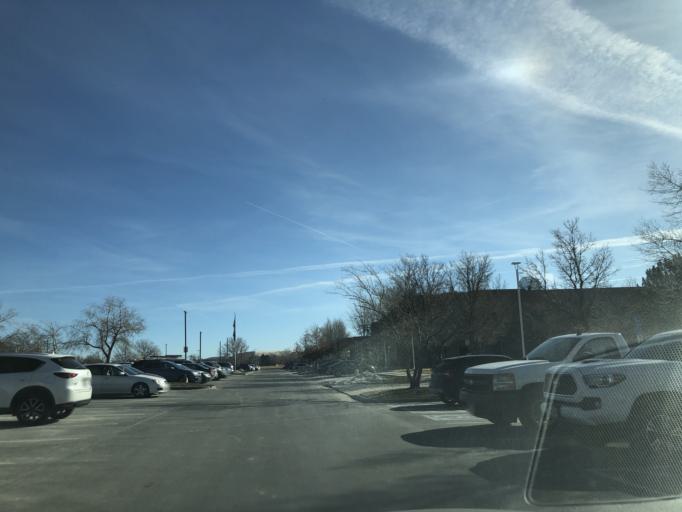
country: US
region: Colorado
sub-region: Adams County
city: Aurora
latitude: 39.7187
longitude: -104.8034
